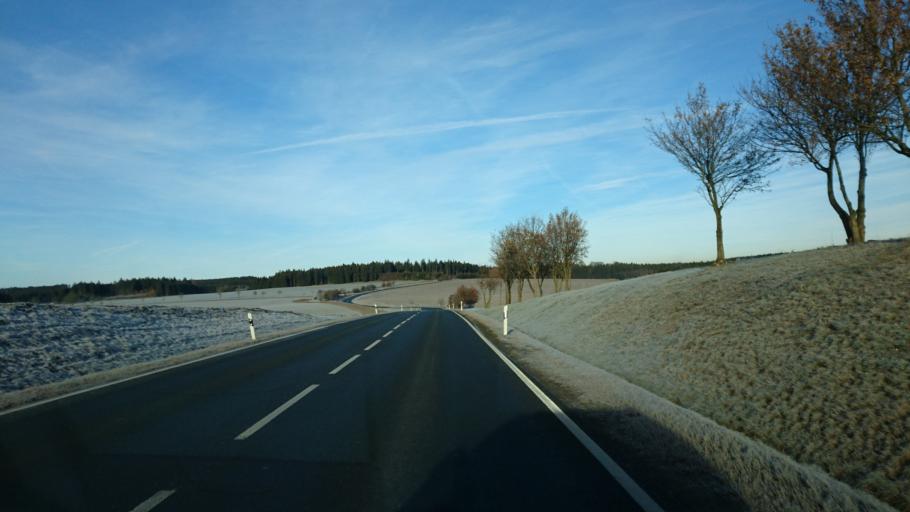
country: DE
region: Thuringia
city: Tanna
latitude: 50.5325
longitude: 11.8710
